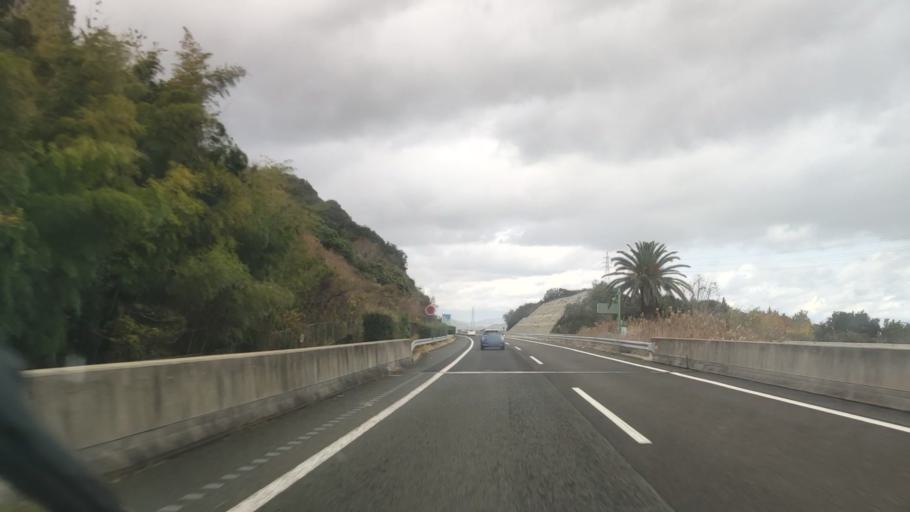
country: JP
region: Tokushima
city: Ishii
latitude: 34.2000
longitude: 134.4302
